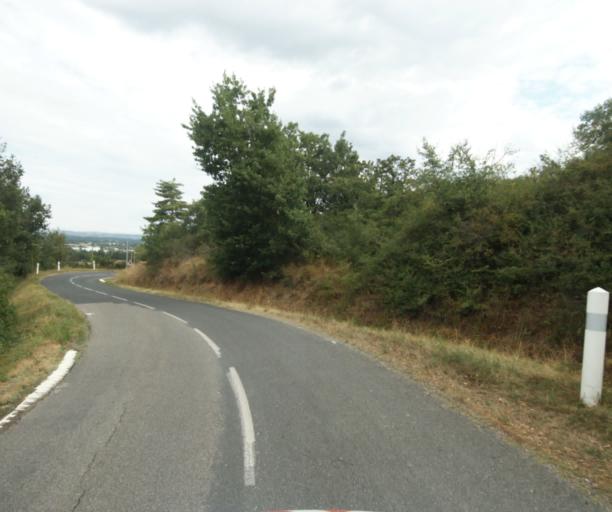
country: FR
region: Midi-Pyrenees
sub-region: Departement de la Haute-Garonne
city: Revel
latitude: 43.4426
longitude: 1.9879
